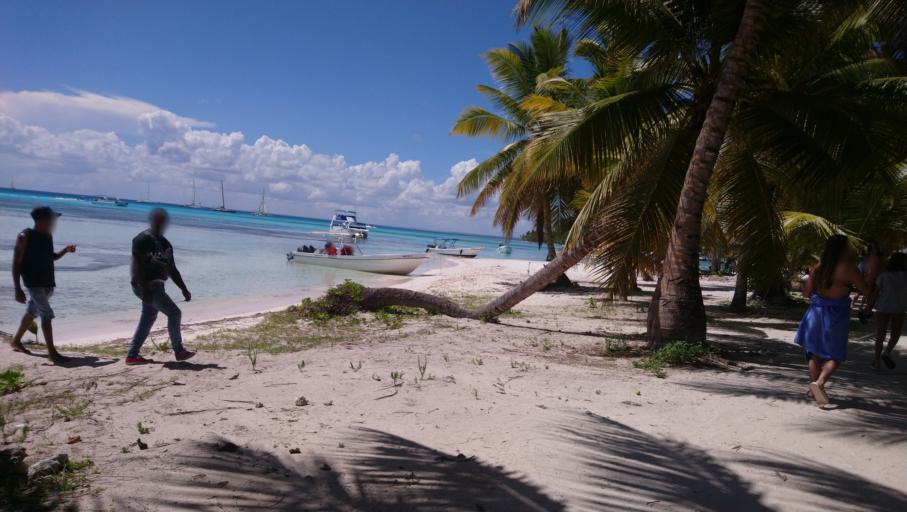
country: DO
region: La Altagracia
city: Boca de Yuma
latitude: 18.1758
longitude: -68.7840
